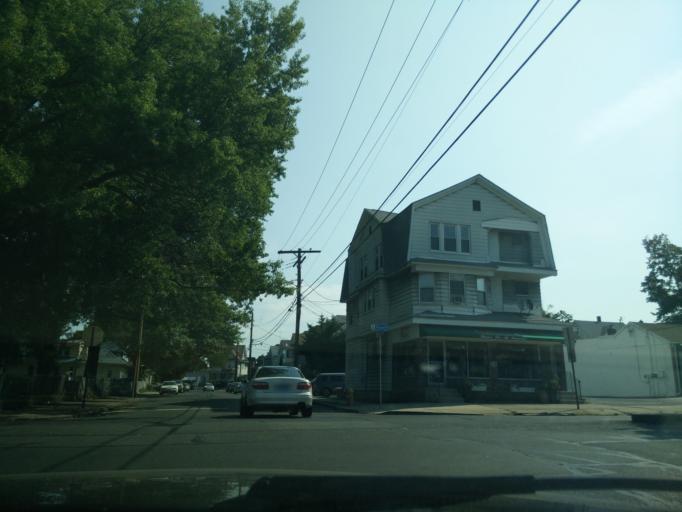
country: US
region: Connecticut
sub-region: Fairfield County
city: Trumbull
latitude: 41.2107
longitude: -73.2095
